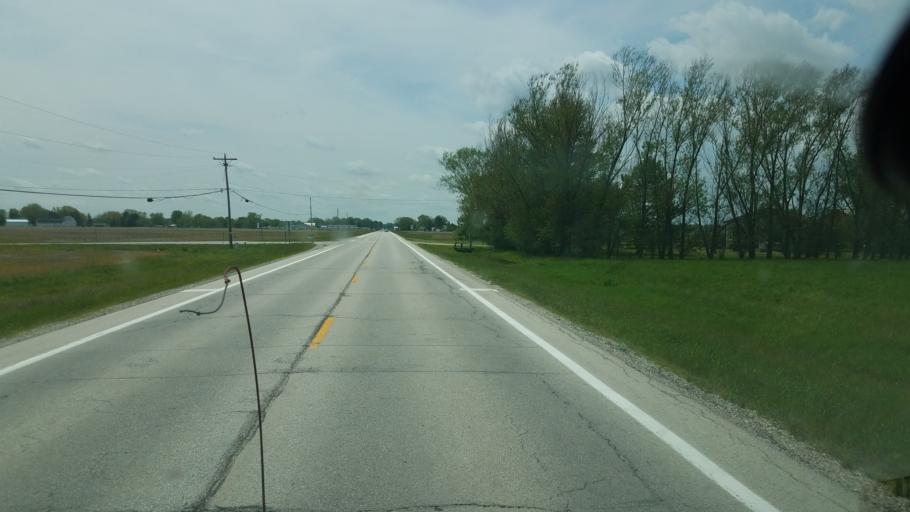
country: US
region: Ohio
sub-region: Sandusky County
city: Fremont
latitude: 41.4291
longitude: -83.0781
